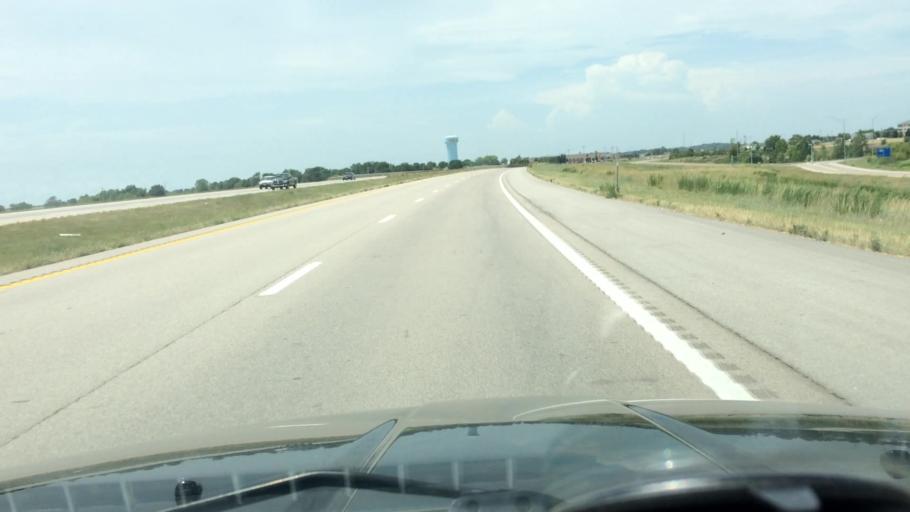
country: US
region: Missouri
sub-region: Polk County
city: Bolivar
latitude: 37.5912
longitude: -93.4297
